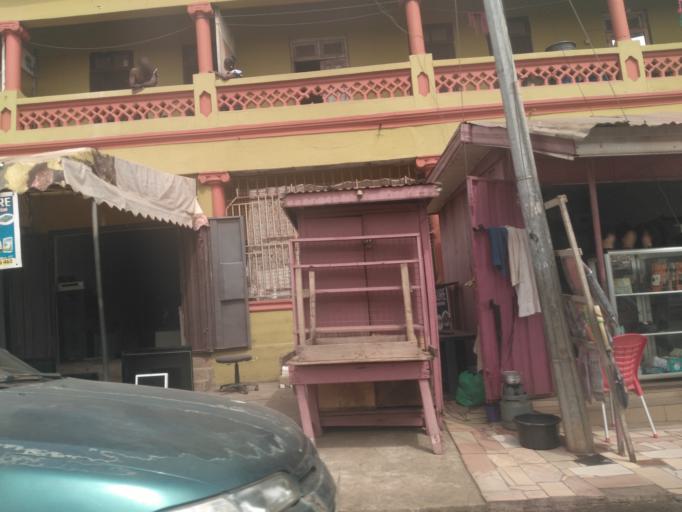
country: GH
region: Ashanti
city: Tafo
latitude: 6.7122
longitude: -1.6156
